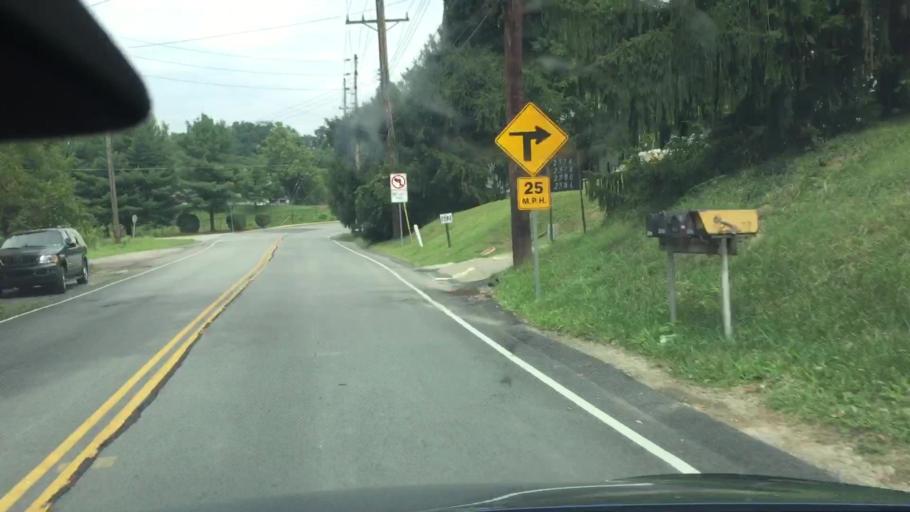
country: US
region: Pennsylvania
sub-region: Allegheny County
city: Monroeville
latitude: 40.4312
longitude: -79.7766
